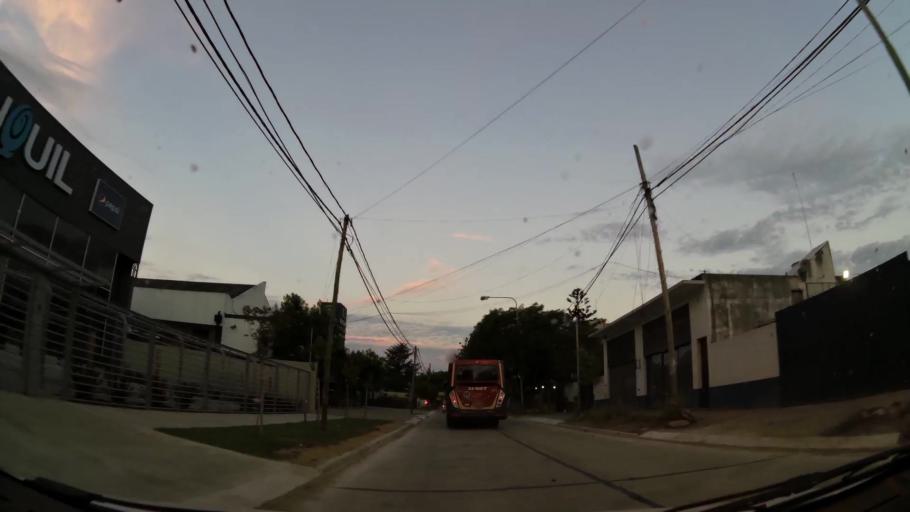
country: AR
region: Buenos Aires
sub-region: Partido de Merlo
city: Merlo
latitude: -34.6659
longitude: -58.7369
